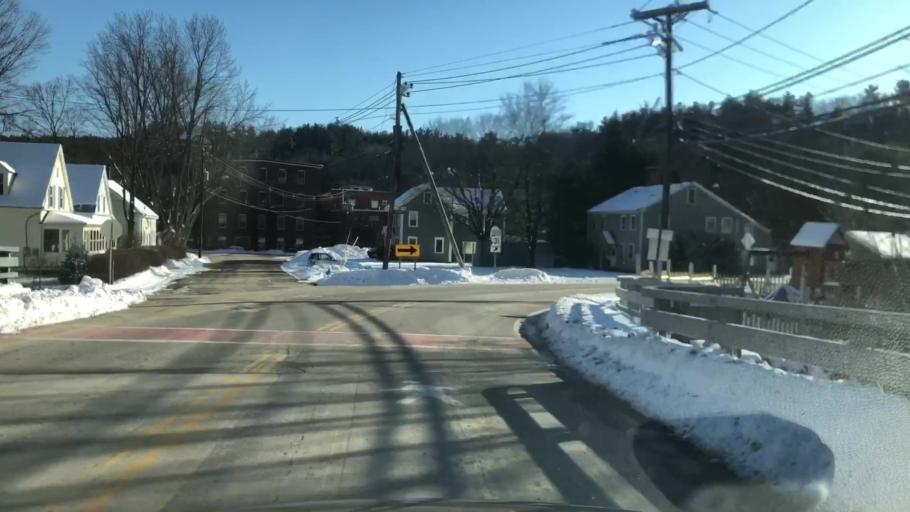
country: US
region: New Hampshire
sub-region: Hillsborough County
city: Wilton
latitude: 42.8439
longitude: -71.7395
